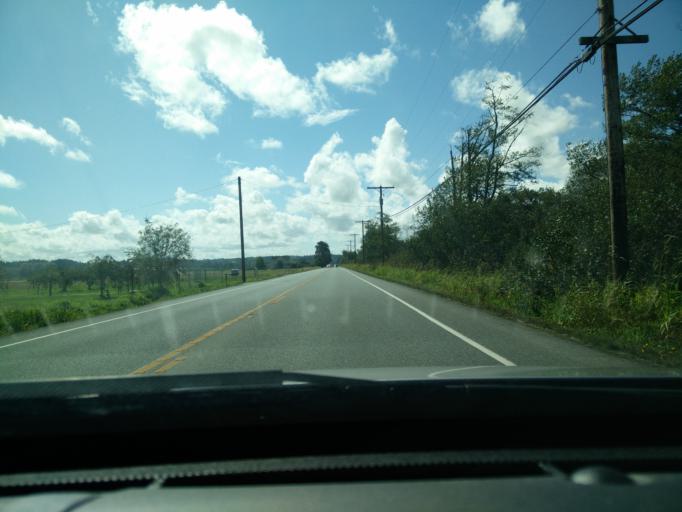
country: US
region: Washington
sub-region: Skagit County
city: Mount Vernon
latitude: 48.3357
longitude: -122.3426
